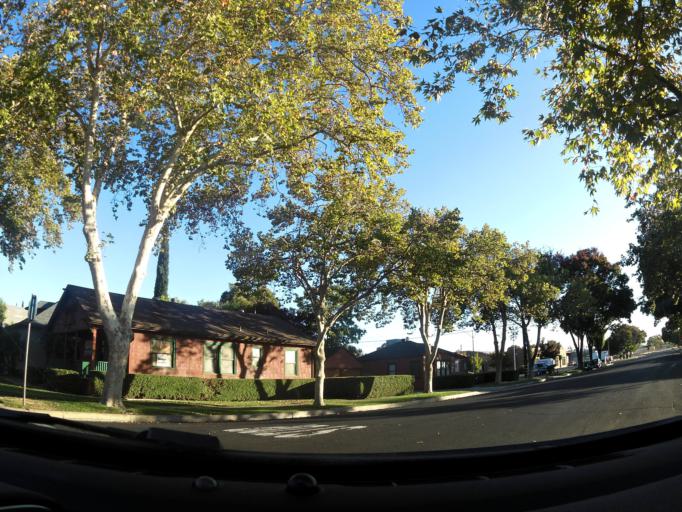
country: US
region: California
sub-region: Merced County
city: Merced
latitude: 37.3046
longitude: -120.4889
